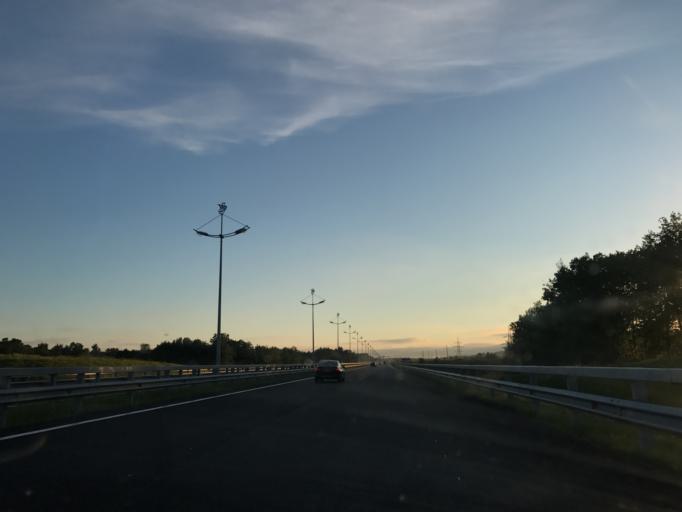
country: RU
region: Kaliningrad
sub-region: Gorod Kaliningrad
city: Pionerskiy
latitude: 54.9213
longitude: 20.3019
